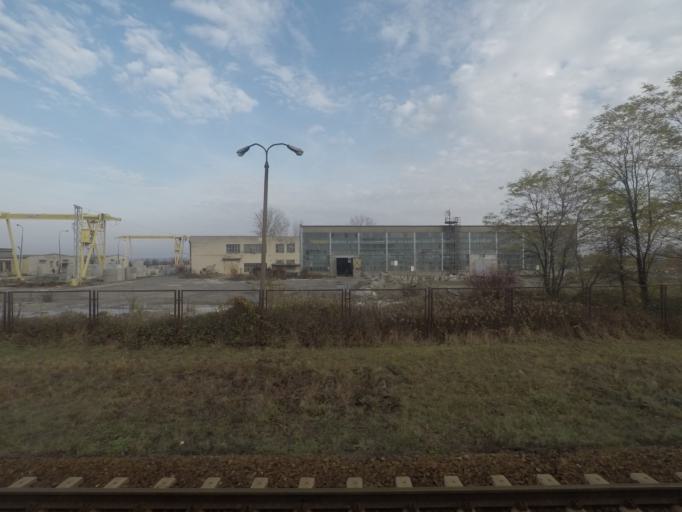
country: PL
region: Subcarpathian Voivodeship
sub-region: Powiat jaroslawski
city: Radymno
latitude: 49.9327
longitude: 22.8375
